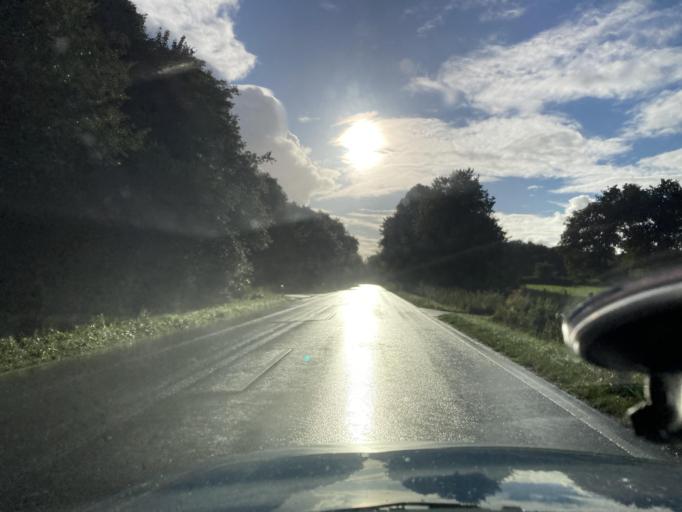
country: DE
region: Schleswig-Holstein
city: Welmbuttel
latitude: 54.2032
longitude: 9.2522
